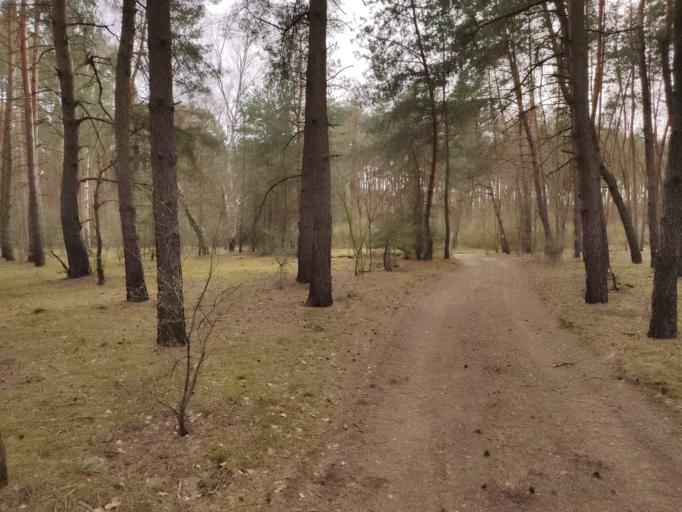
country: PL
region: Greater Poland Voivodeship
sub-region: Powiat sredzki
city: Sroda Wielkopolska
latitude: 52.1453
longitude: 17.2704
